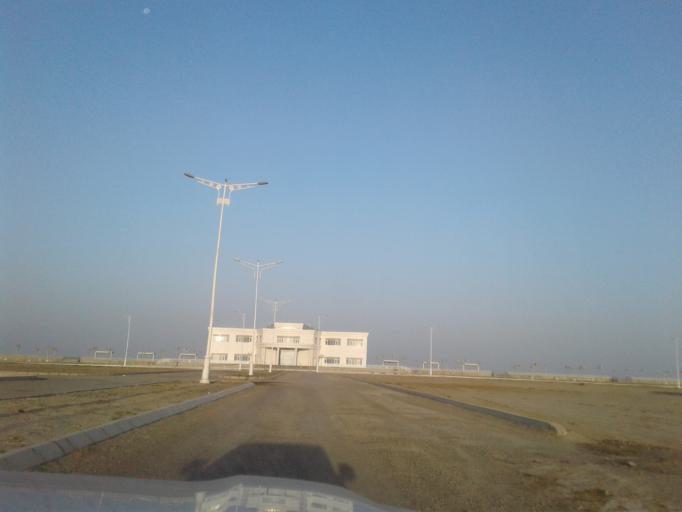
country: IR
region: Golestan
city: Aq Qayeh
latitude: 37.7056
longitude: 54.7438
